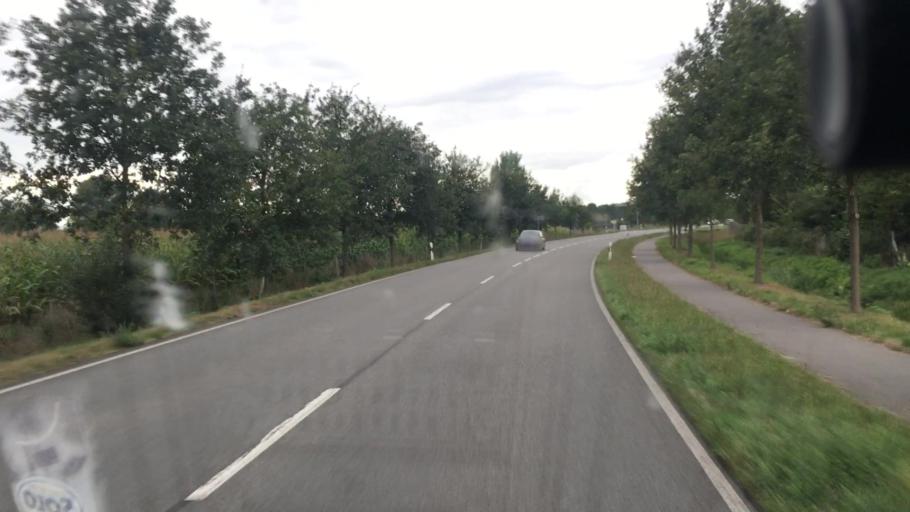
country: DE
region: Lower Saxony
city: Lohne
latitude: 52.6500
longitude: 8.2049
